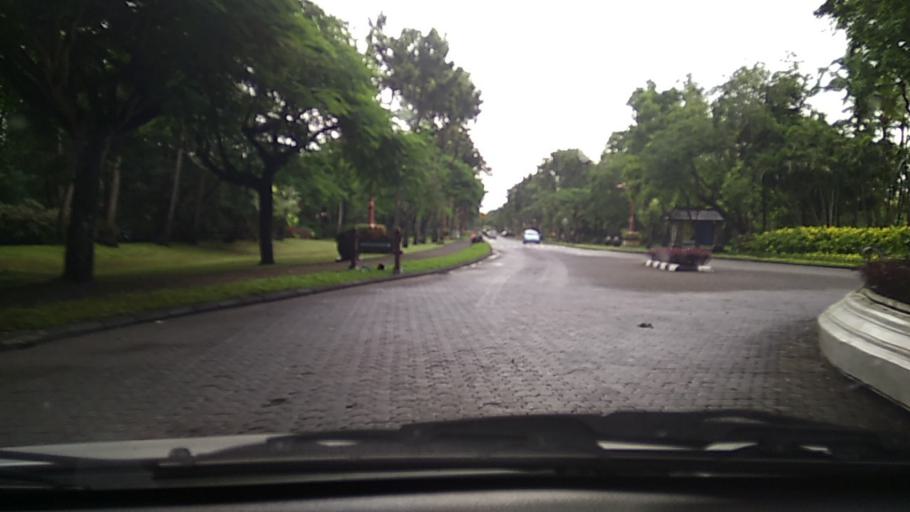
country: ID
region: Bali
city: Bualu
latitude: -8.8039
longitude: 115.2288
